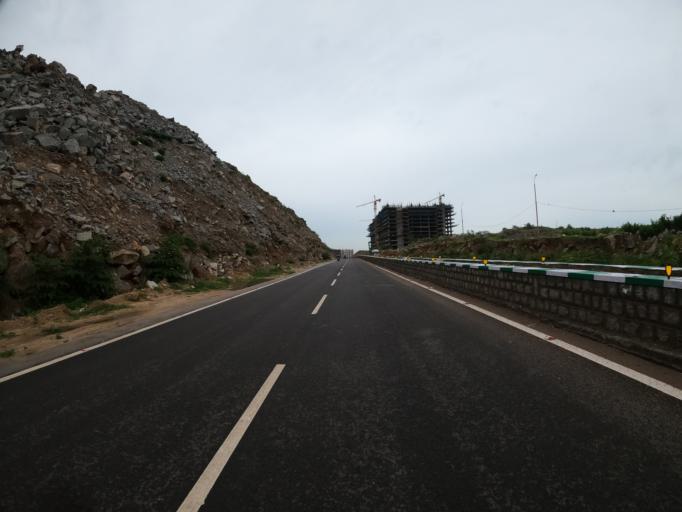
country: IN
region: Telangana
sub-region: Rangareddi
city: Kukatpalli
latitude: 17.4635
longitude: 78.3810
